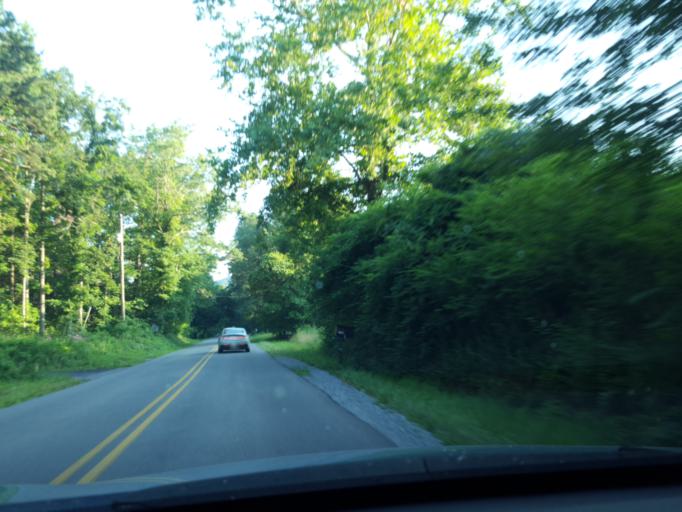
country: US
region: Virginia
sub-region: Augusta County
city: Lyndhurst
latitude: 37.9655
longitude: -78.9604
